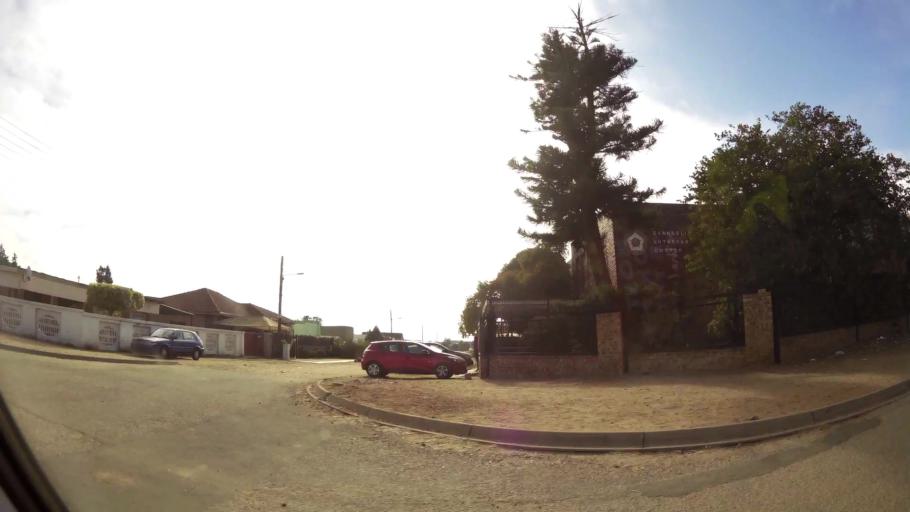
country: ZA
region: Limpopo
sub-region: Capricorn District Municipality
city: Polokwane
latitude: -23.8457
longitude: 29.3851
